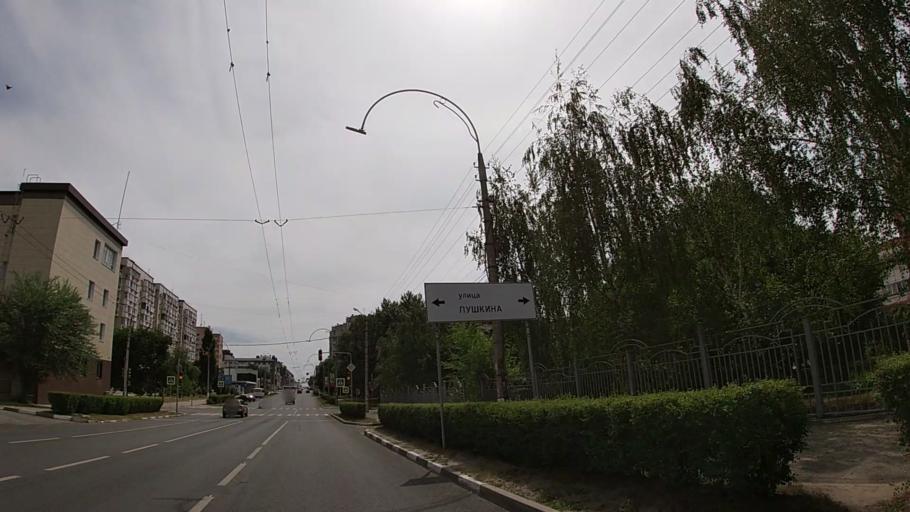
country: RU
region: Belgorod
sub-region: Belgorodskiy Rayon
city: Belgorod
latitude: 50.5992
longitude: 36.5764
